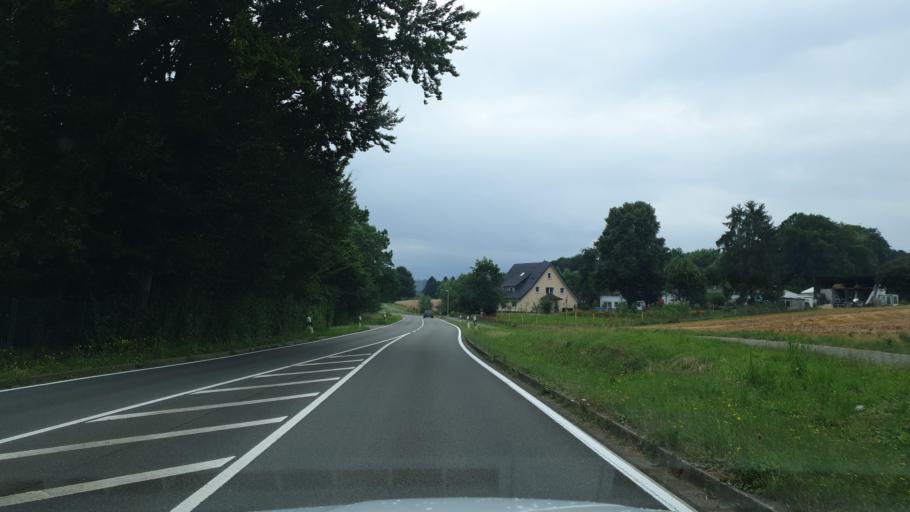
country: DE
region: North Rhine-Westphalia
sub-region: Regierungsbezirk Detmold
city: Bad Salzuflen
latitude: 52.1311
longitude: 8.7774
